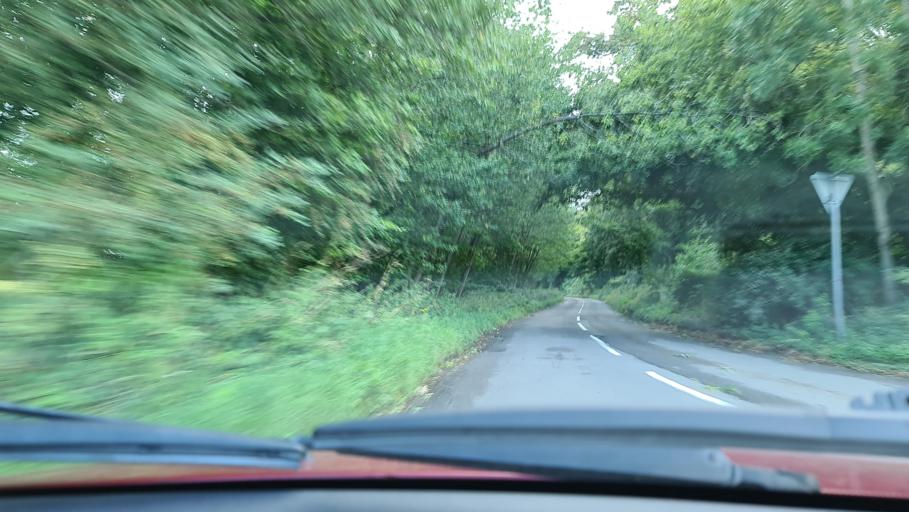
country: GB
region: England
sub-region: Buckinghamshire
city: Wendover
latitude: 51.7271
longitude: -0.7782
